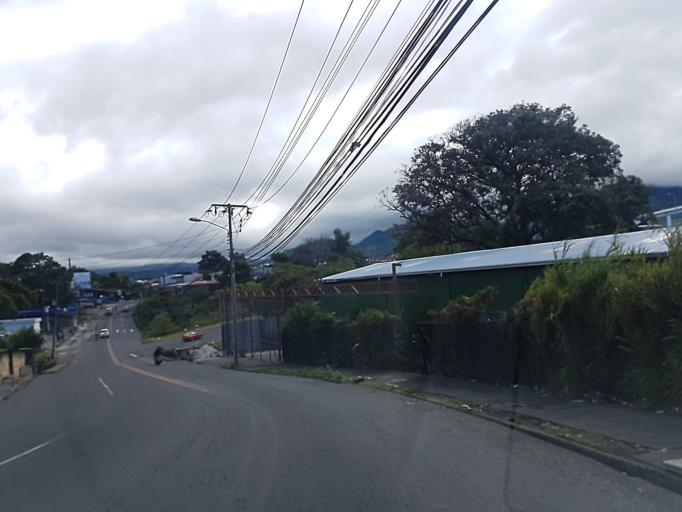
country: CR
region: San Jose
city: San Jose
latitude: 9.9219
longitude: -84.0947
